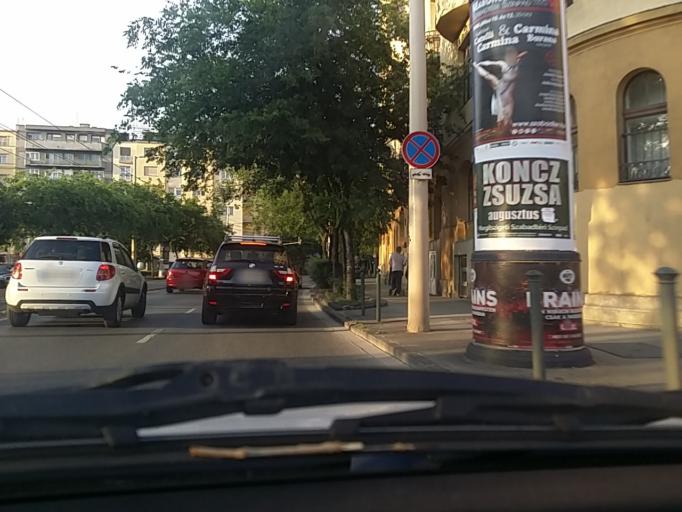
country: HU
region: Budapest
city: Budapest II. keruelet
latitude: 47.5093
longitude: 19.0283
